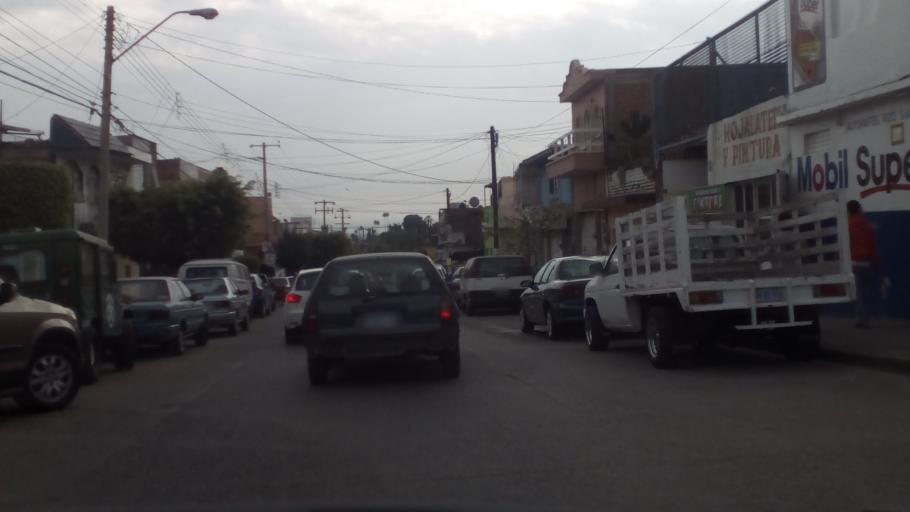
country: MX
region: Guanajuato
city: Leon
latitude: 21.1310
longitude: -101.6966
